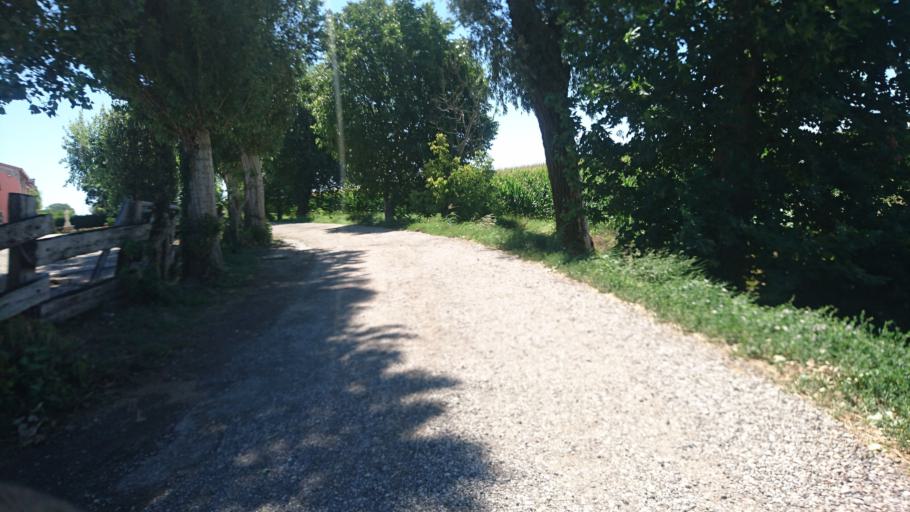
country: IT
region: Veneto
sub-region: Provincia di Padova
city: Pontelongo
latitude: 45.2575
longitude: 12.0162
